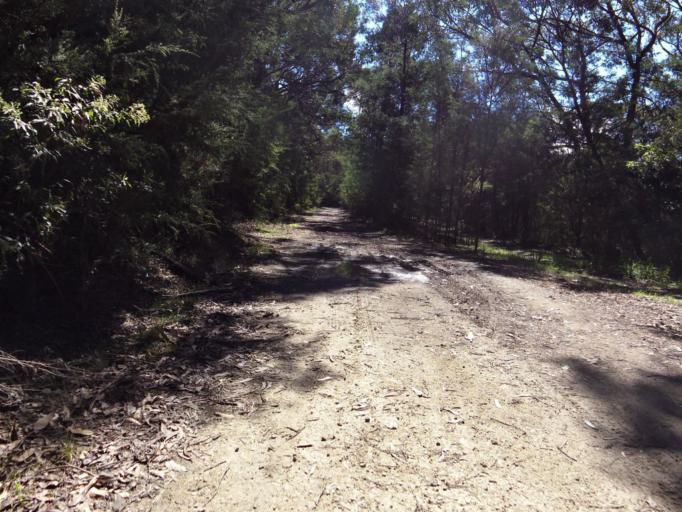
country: AU
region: Victoria
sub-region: Latrobe
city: Moe
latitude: -38.1714
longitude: 146.3314
